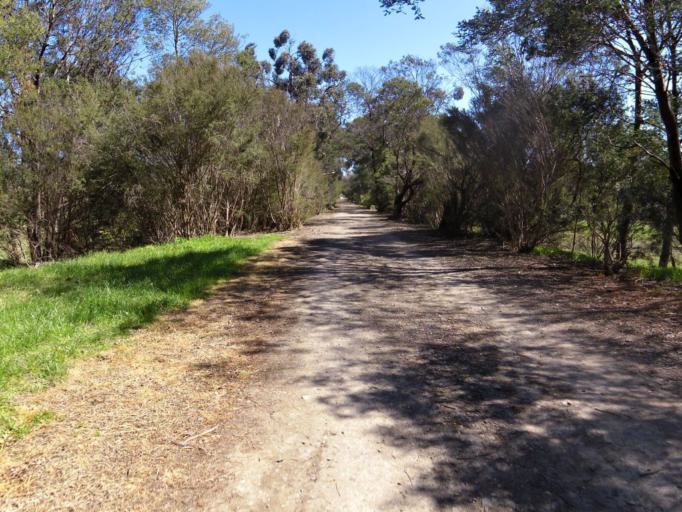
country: AU
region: Victoria
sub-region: Latrobe
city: Moe
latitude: -38.1750
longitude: 146.2757
